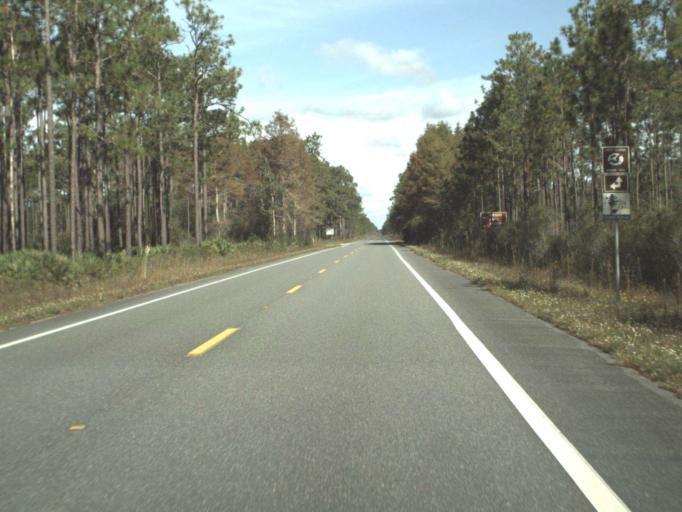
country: US
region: Florida
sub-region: Gulf County
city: Wewahitchka
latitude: 29.9907
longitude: -84.9765
